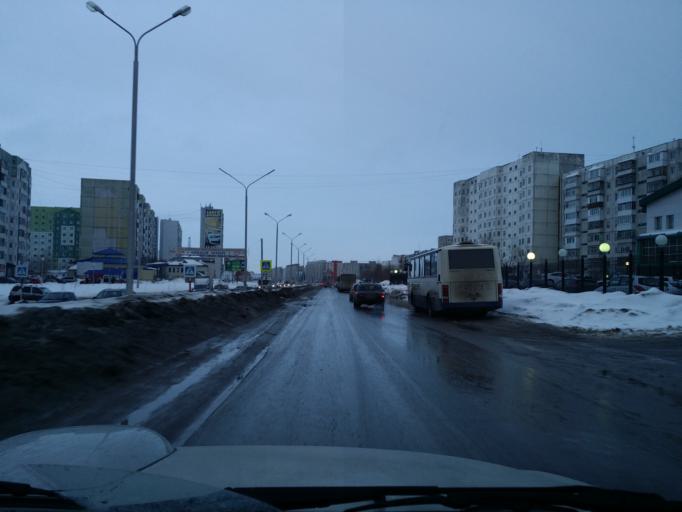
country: RU
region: Khanty-Mansiyskiy Avtonomnyy Okrug
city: Nizhnevartovsk
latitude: 60.9486
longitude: 76.5914
